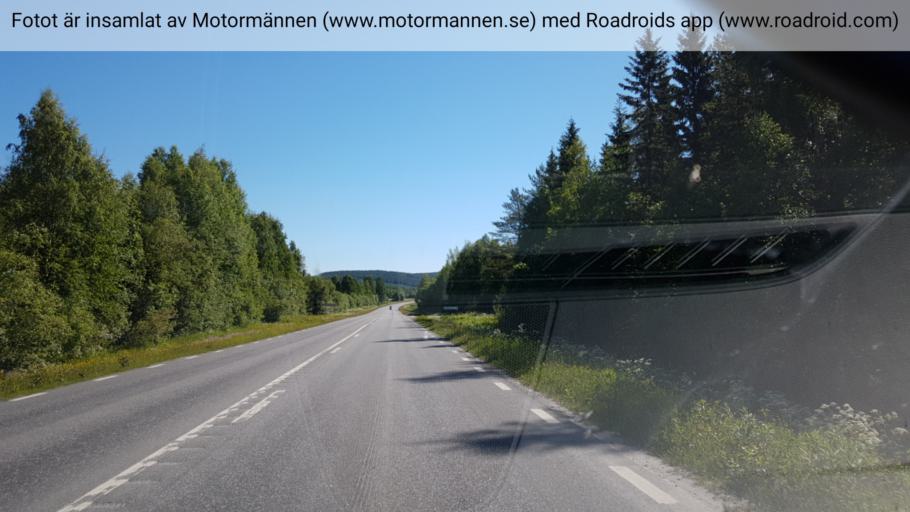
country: SE
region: Norrbotten
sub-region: Bodens Kommun
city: Boden
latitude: 65.8500
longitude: 21.5456
